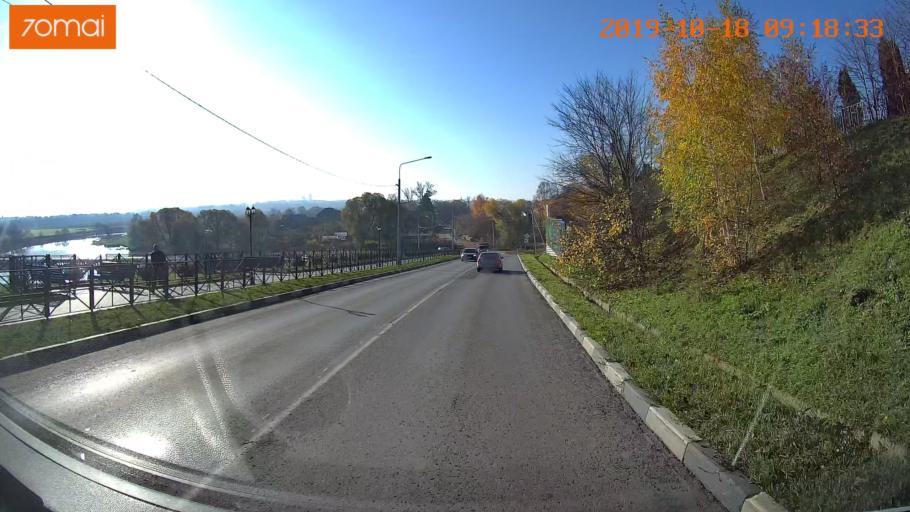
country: RU
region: Tula
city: Yefremov
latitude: 53.1362
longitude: 38.1205
